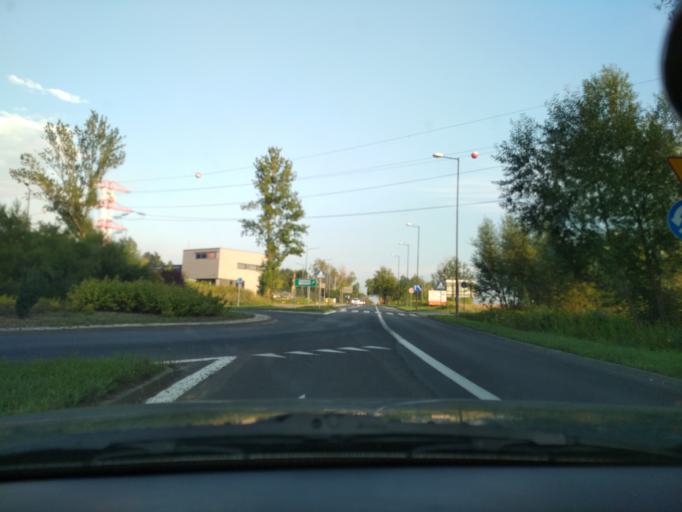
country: PL
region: Silesian Voivodeship
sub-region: Gliwice
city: Gliwice
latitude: 50.2716
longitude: 18.6856
